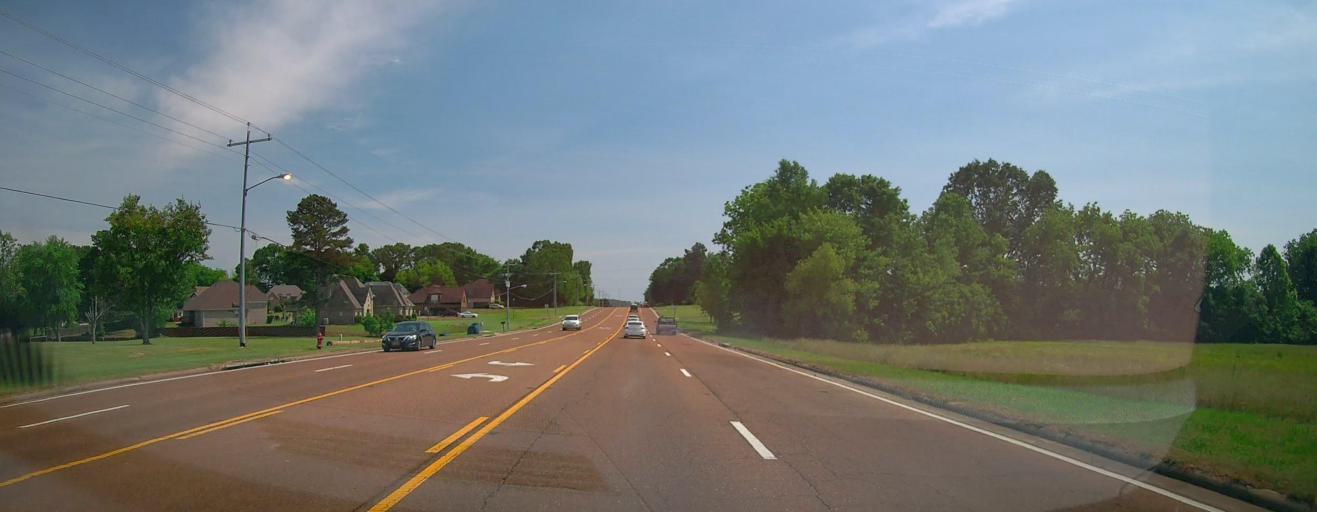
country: US
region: Mississippi
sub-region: De Soto County
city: Olive Branch
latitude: 34.9814
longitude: -89.8306
